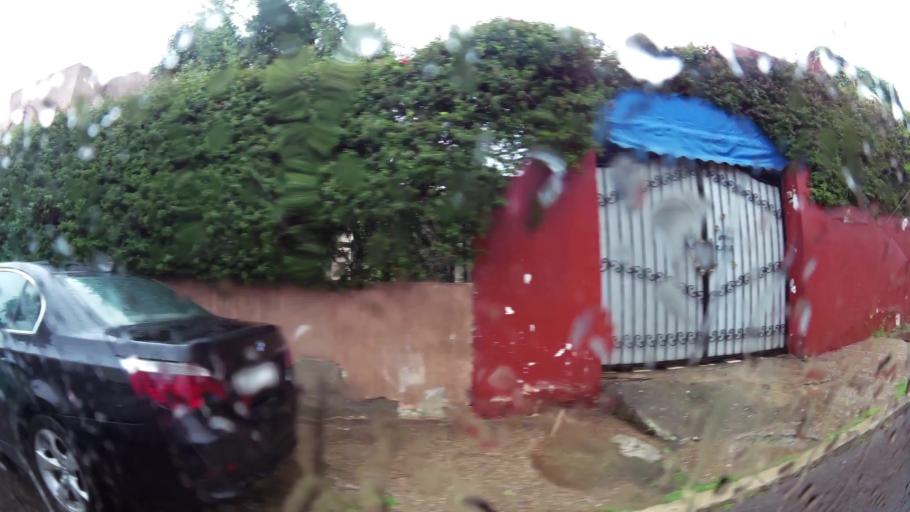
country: MA
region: Grand Casablanca
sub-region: Casablanca
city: Casablanca
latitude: 33.5711
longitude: -7.6326
